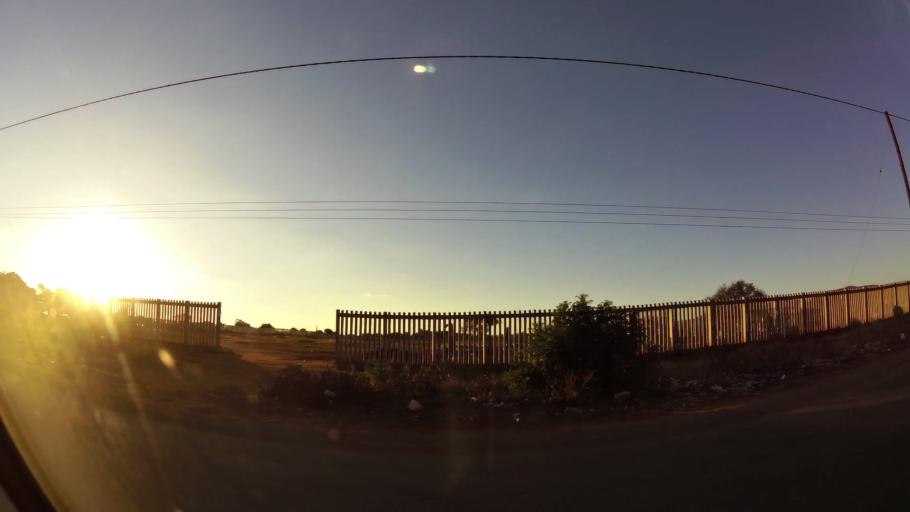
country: ZA
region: Limpopo
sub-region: Waterberg District Municipality
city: Mokopane
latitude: -24.1385
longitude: 28.9823
